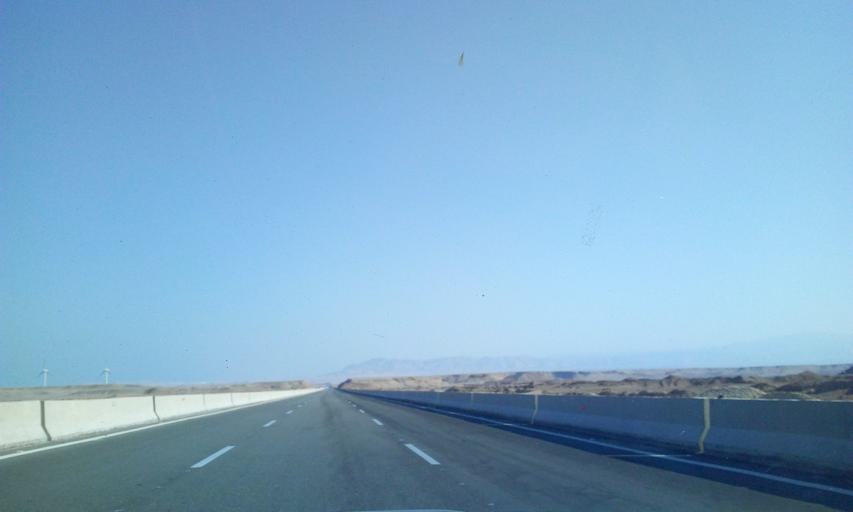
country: EG
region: As Suways
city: Ain Sukhna
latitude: 29.1710
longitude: 32.5068
